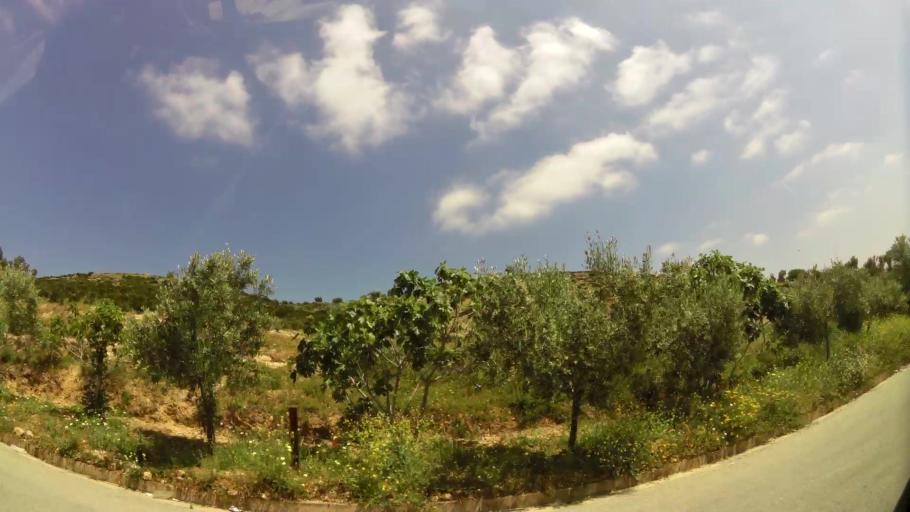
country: MA
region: Fes-Boulemane
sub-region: Fes
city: Fes
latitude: 34.0634
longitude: -5.0264
